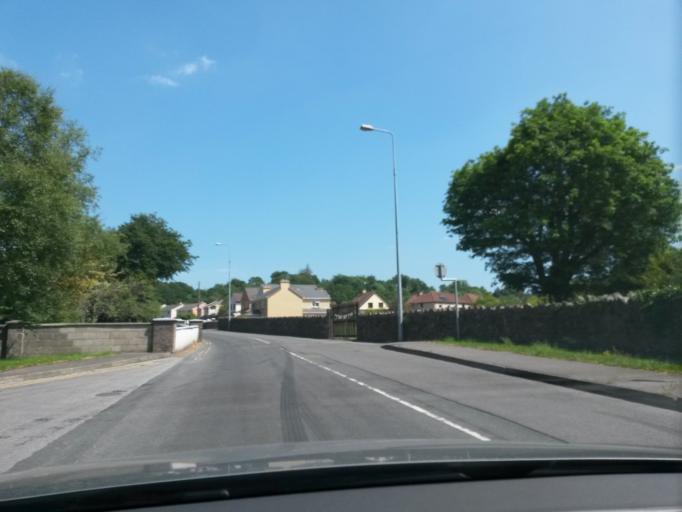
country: IE
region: Munster
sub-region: Ciarrai
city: Cill Airne
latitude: 52.0572
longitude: -9.4751
